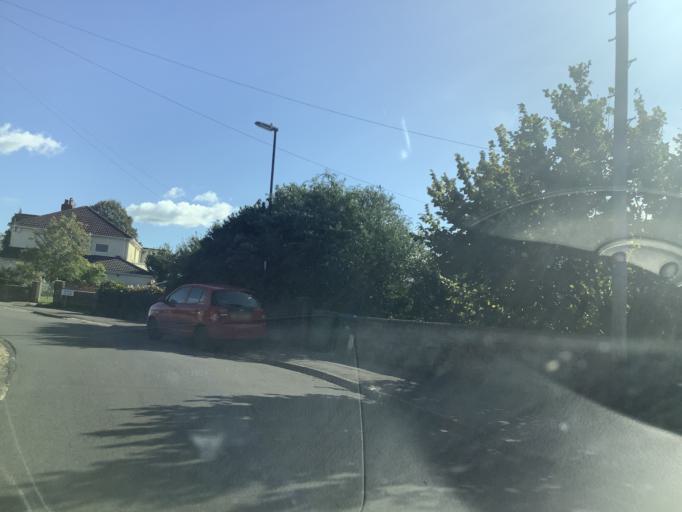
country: GB
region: England
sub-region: Hampshire
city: Marchwood
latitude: 50.9309
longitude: -1.4441
